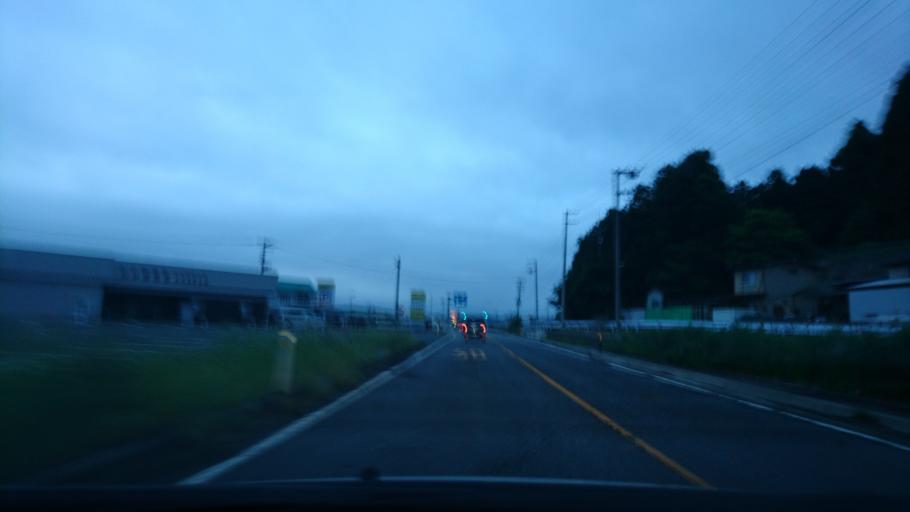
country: JP
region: Iwate
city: Ichinoseki
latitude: 38.8056
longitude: 141.0713
